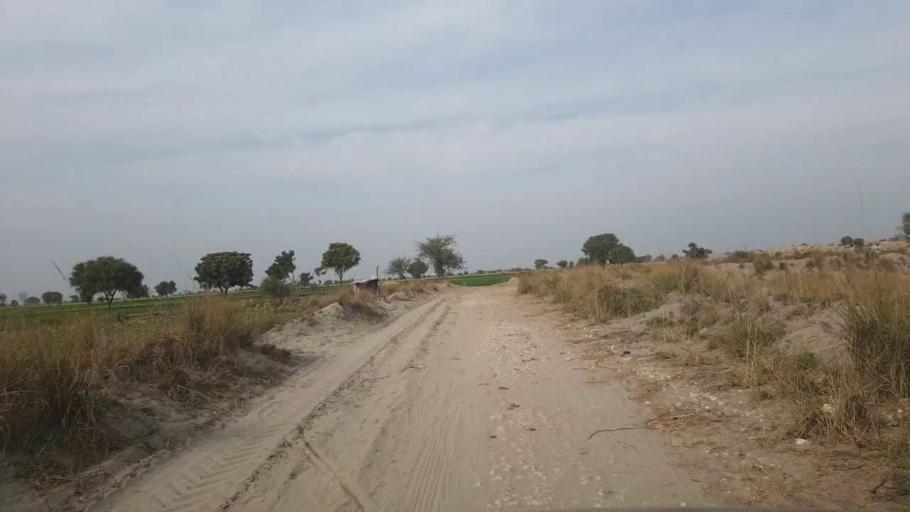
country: PK
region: Sindh
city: Shahpur Chakar
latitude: 26.1163
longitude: 68.5082
